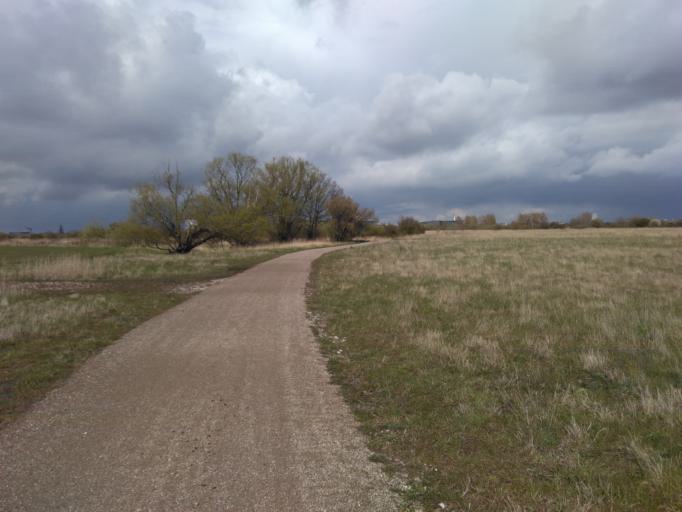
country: DK
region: Capital Region
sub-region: Kobenhavn
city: Copenhagen
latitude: 55.6442
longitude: 12.5700
